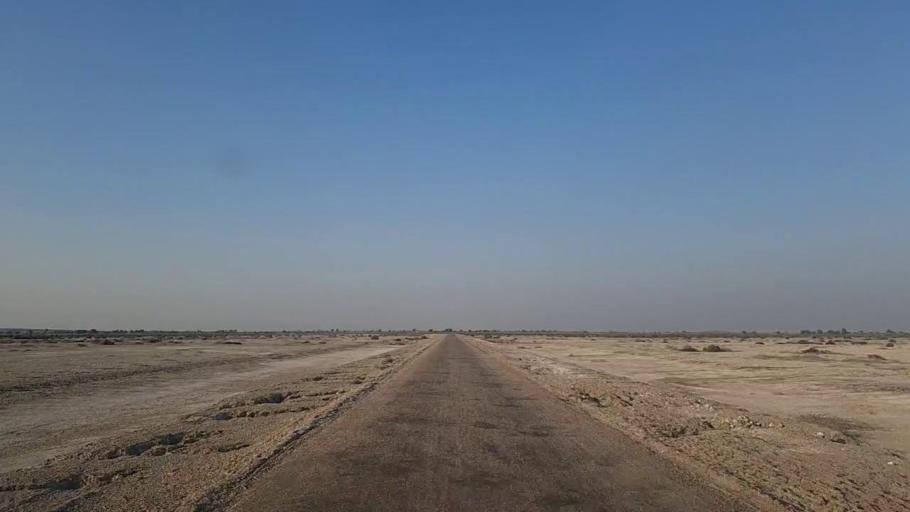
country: PK
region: Sindh
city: Jam Sahib
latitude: 26.3180
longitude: 68.6688
